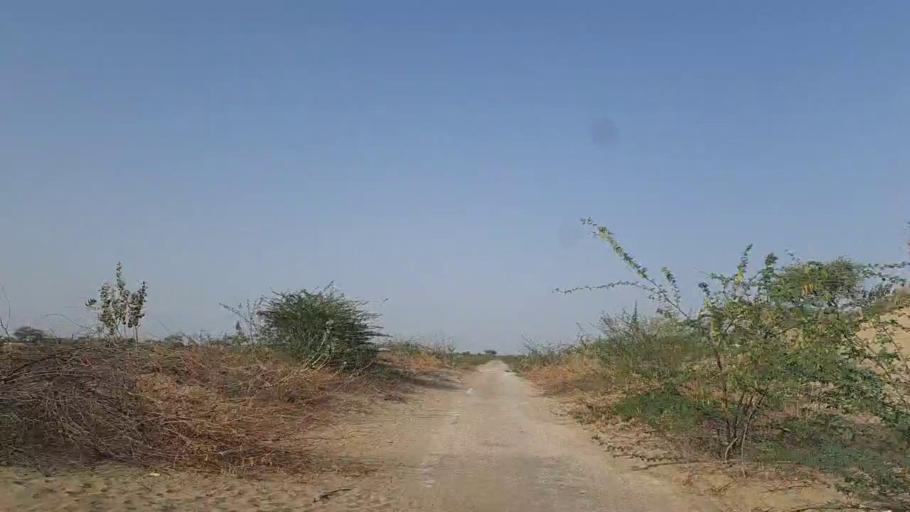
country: PK
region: Sindh
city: Naukot
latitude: 24.6169
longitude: 69.3474
